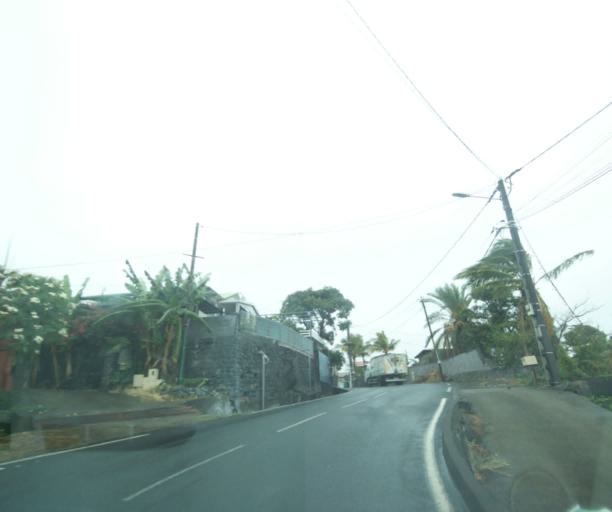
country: RE
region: Reunion
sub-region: Reunion
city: Saint-Paul
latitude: -21.0206
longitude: 55.2888
